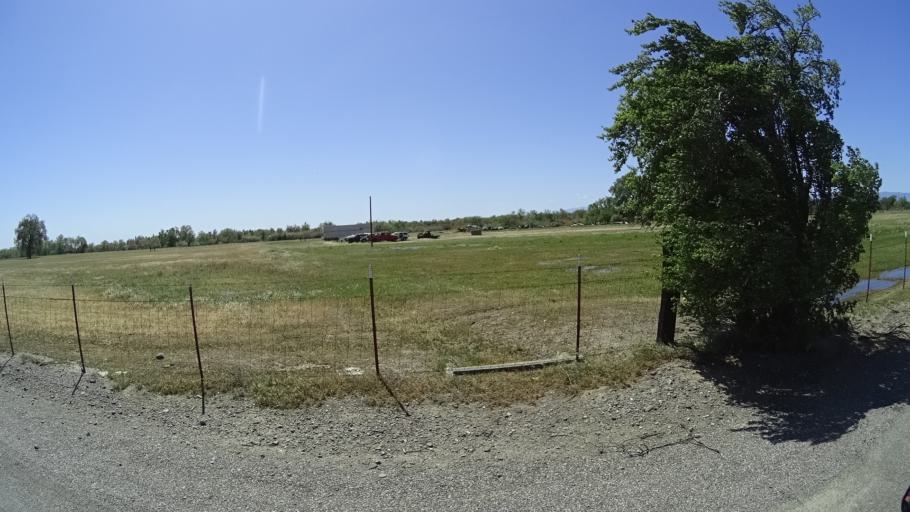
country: US
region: California
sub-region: Glenn County
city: Orland
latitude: 39.7970
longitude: -122.2537
